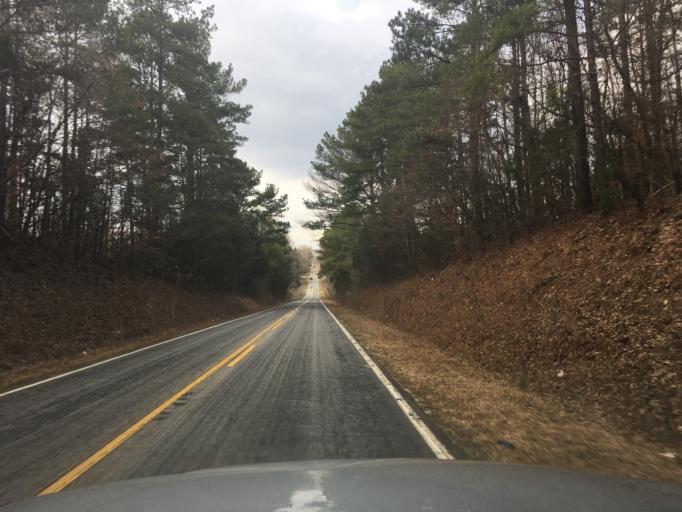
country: US
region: South Carolina
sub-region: Abbeville County
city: Due West
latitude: 34.2574
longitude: -82.4163
